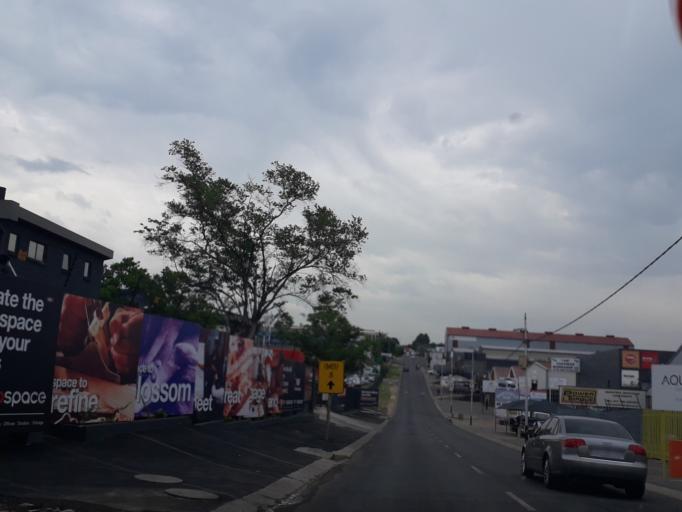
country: ZA
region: Gauteng
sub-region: City of Johannesburg Metropolitan Municipality
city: Modderfontein
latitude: -26.1050
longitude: 28.0818
